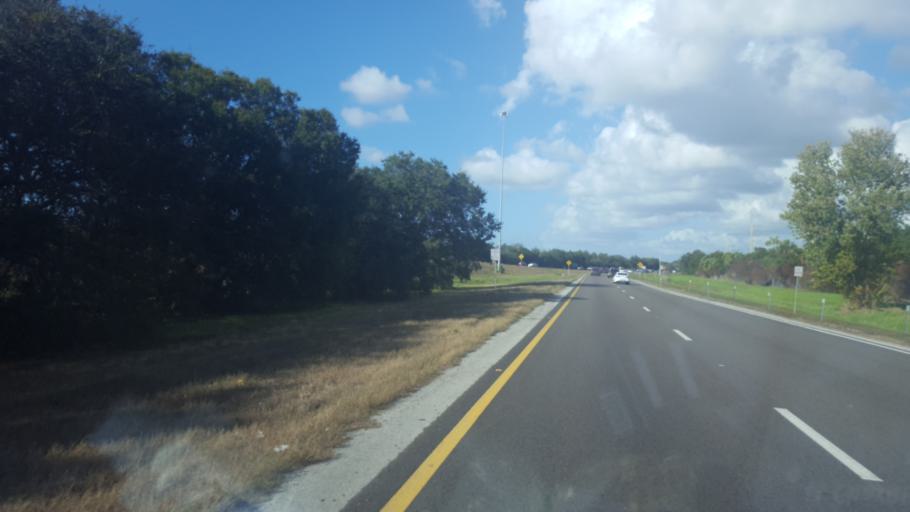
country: US
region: Florida
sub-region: Sarasota County
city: Lake Sarasota
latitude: 27.2702
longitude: -82.4479
